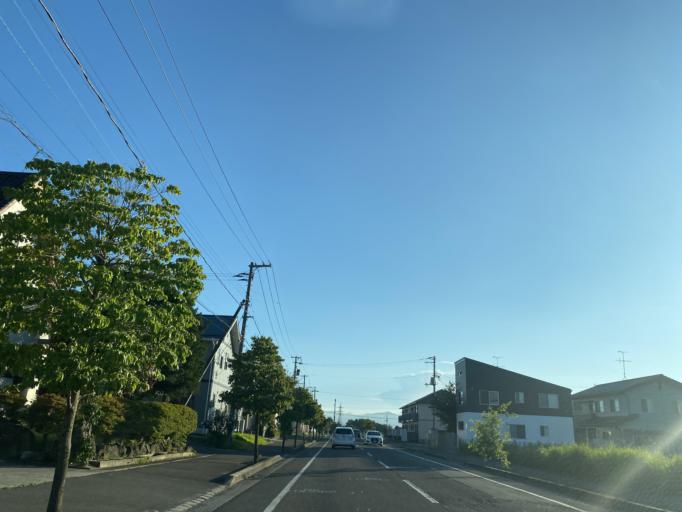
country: JP
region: Fukushima
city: Koriyama
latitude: 37.4366
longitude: 140.3837
